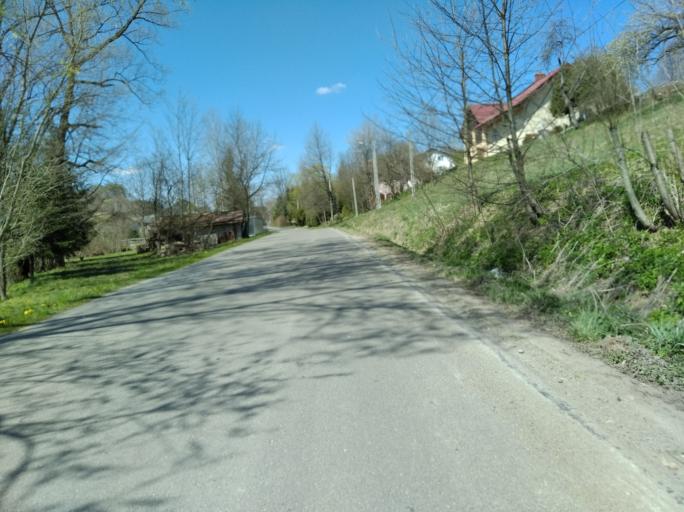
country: PL
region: Subcarpathian Voivodeship
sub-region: Powiat brzozowski
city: Jablonka
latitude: 49.7120
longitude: 22.1396
